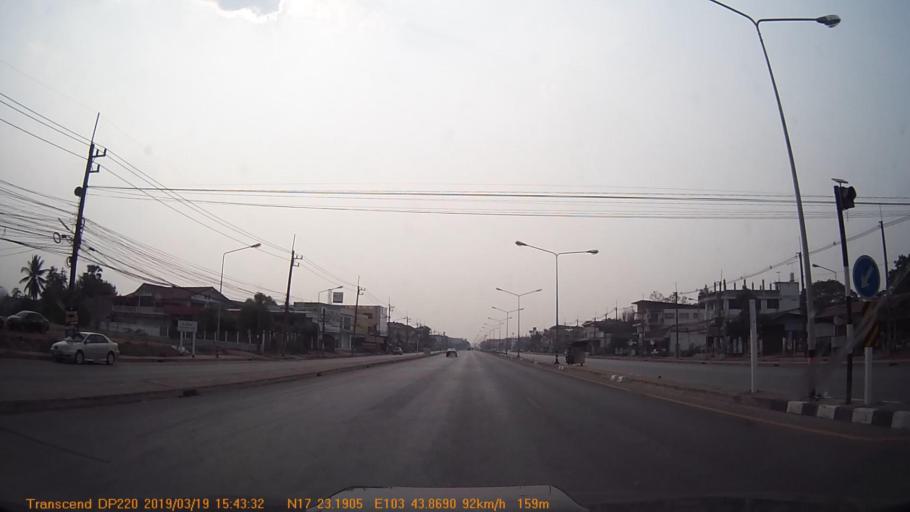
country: TH
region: Sakon Nakhon
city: Phang Khon
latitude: 17.3866
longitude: 103.7309
